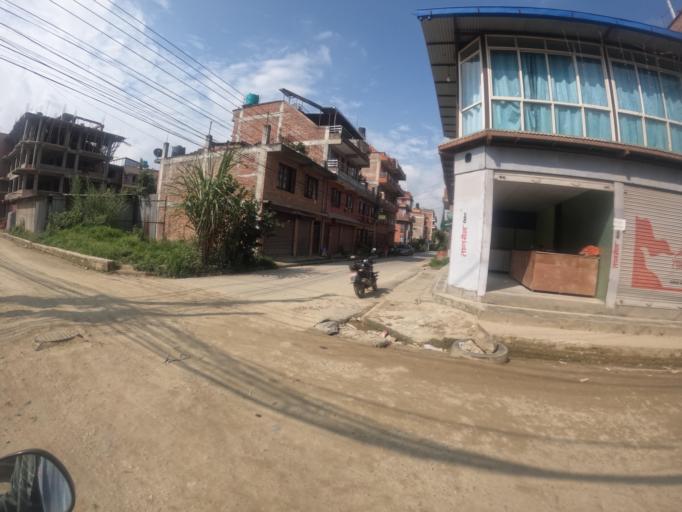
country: NP
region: Central Region
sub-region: Bagmati Zone
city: Bhaktapur
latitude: 27.6778
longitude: 85.4424
